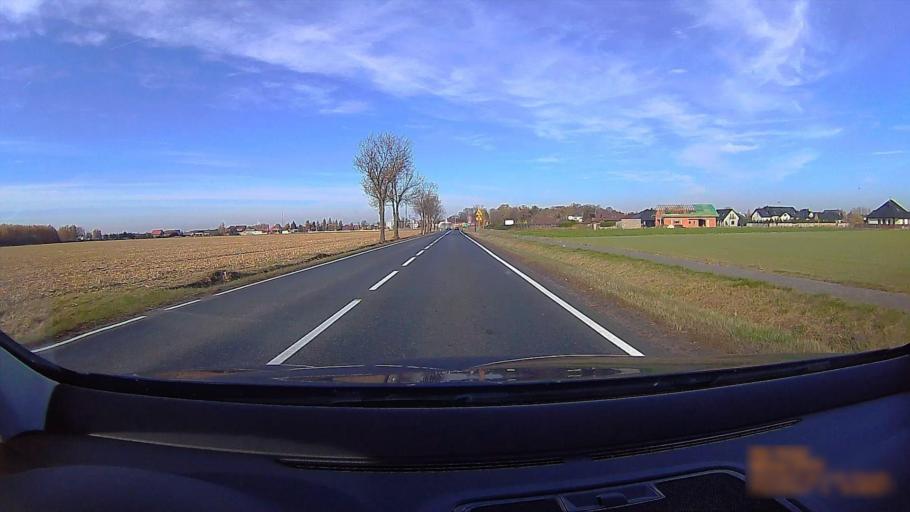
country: PL
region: Greater Poland Voivodeship
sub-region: Powiat koninski
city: Rychwal
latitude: 52.0625
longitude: 18.1638
